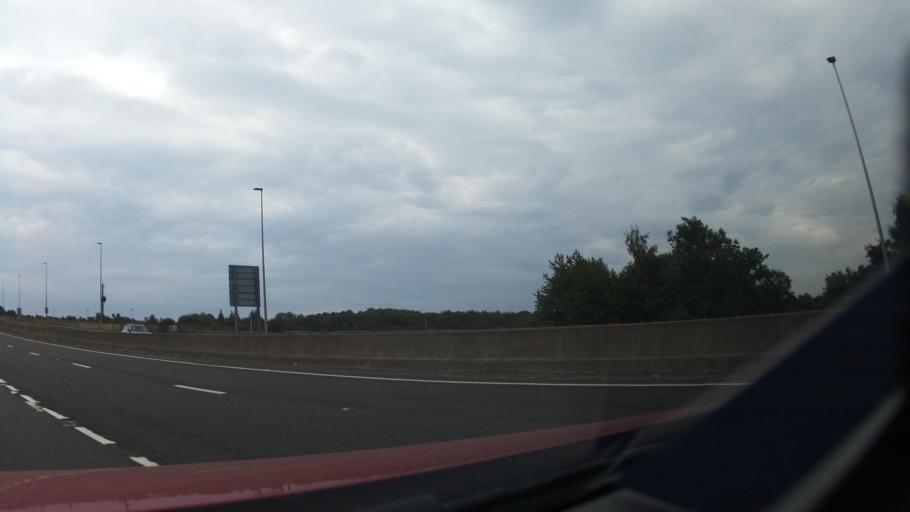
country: GB
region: Scotland
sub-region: South Lanarkshire
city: Bothwell
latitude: 55.8063
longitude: -4.0479
